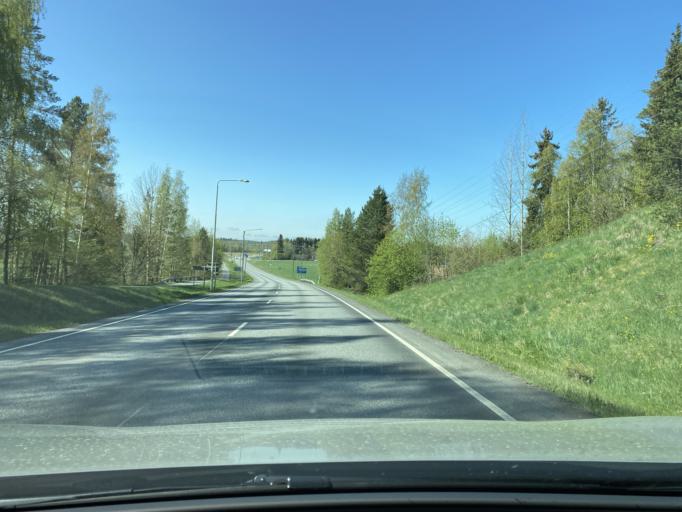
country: FI
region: Pirkanmaa
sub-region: Lounais-Pirkanmaa
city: Vammala
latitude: 61.3541
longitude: 22.8767
